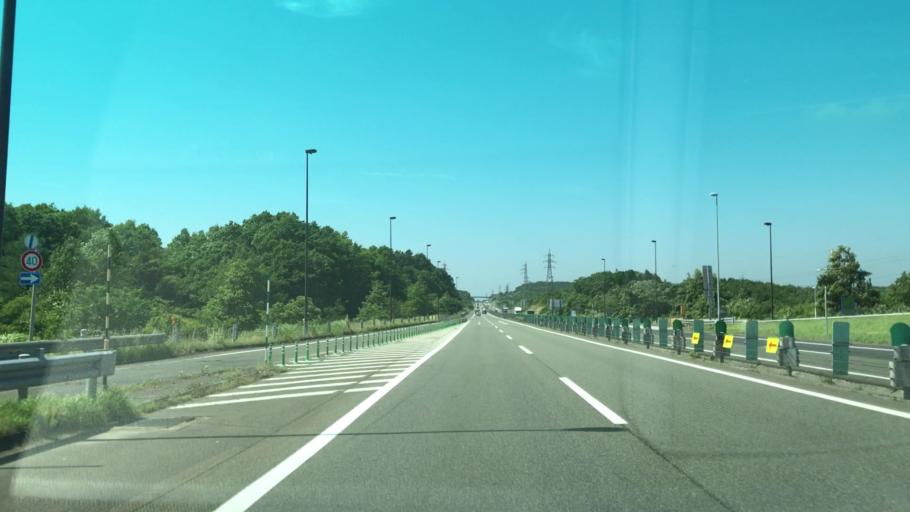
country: JP
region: Hokkaido
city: Kitahiroshima
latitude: 42.9525
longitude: 141.5107
